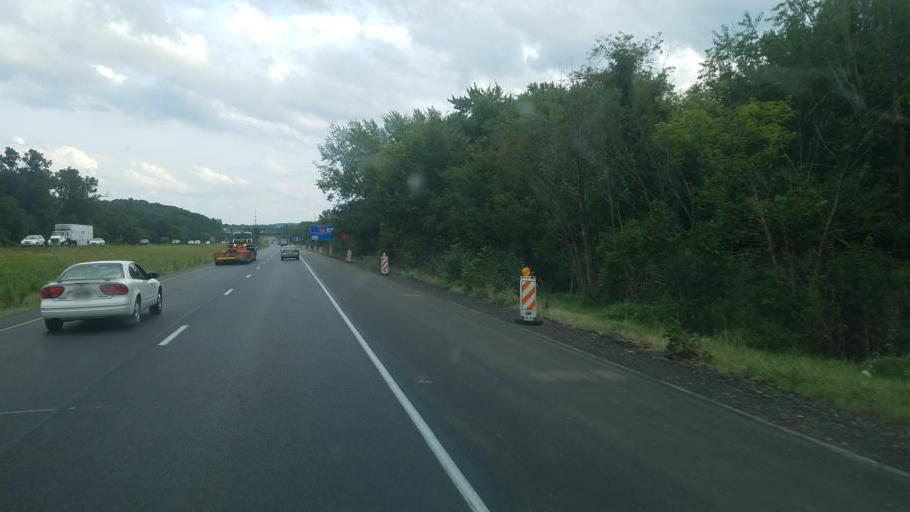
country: US
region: Pennsylvania
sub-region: Butler County
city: Fox Run
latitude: 40.7088
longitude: -80.1021
